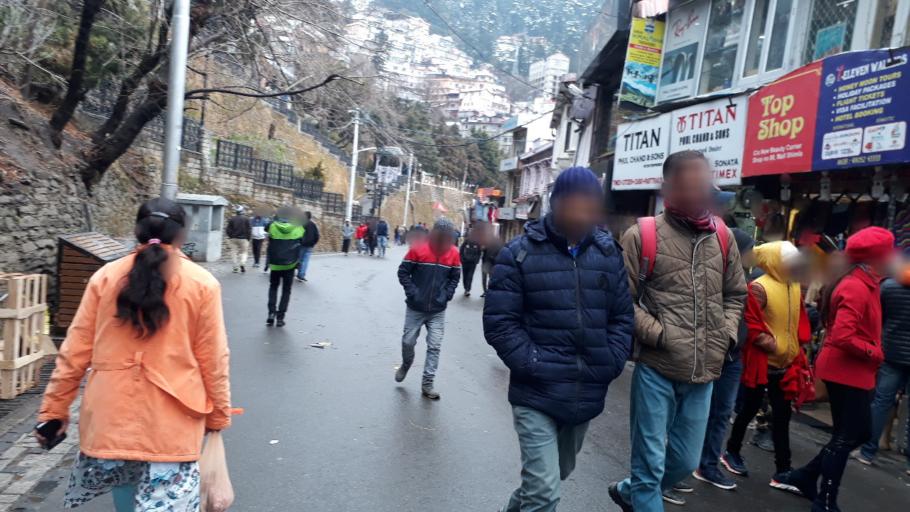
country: IN
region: Himachal Pradesh
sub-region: Shimla
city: Shimla
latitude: 31.1039
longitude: 77.1758
